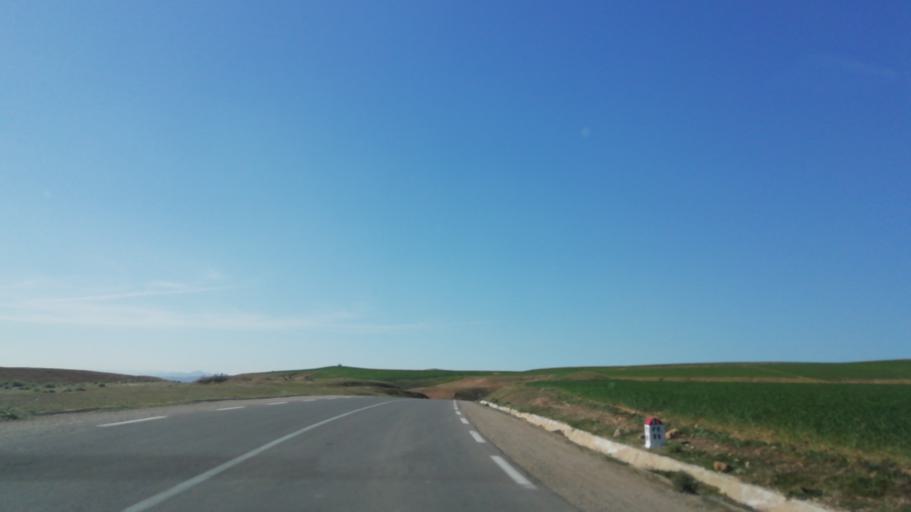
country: DZ
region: Mascara
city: Oued el Abtal
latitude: 35.4479
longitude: 0.8141
